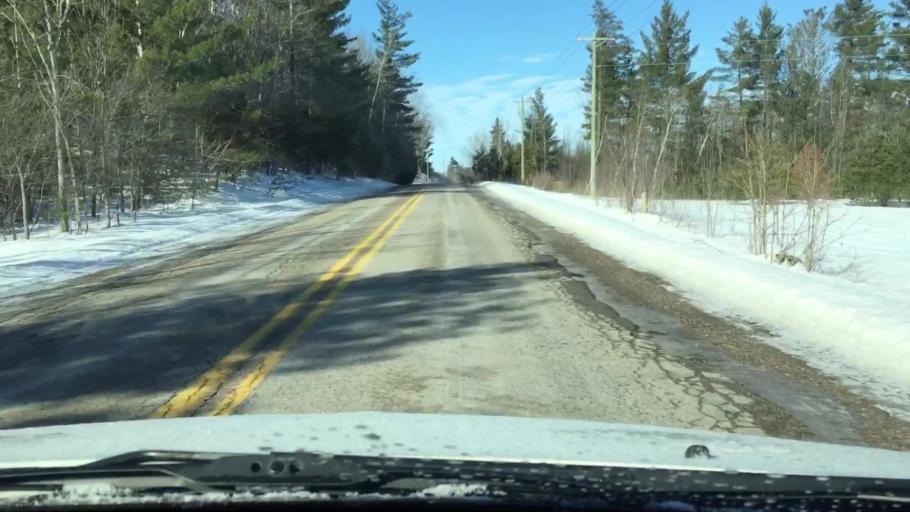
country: US
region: Michigan
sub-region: Charlevoix County
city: East Jordan
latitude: 45.1080
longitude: -85.1288
